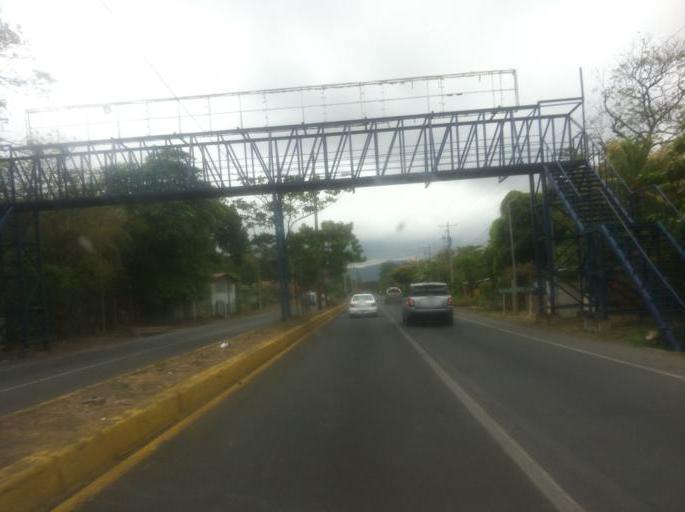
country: NI
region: Masaya
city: Ticuantepe
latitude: 12.0249
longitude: -86.1680
